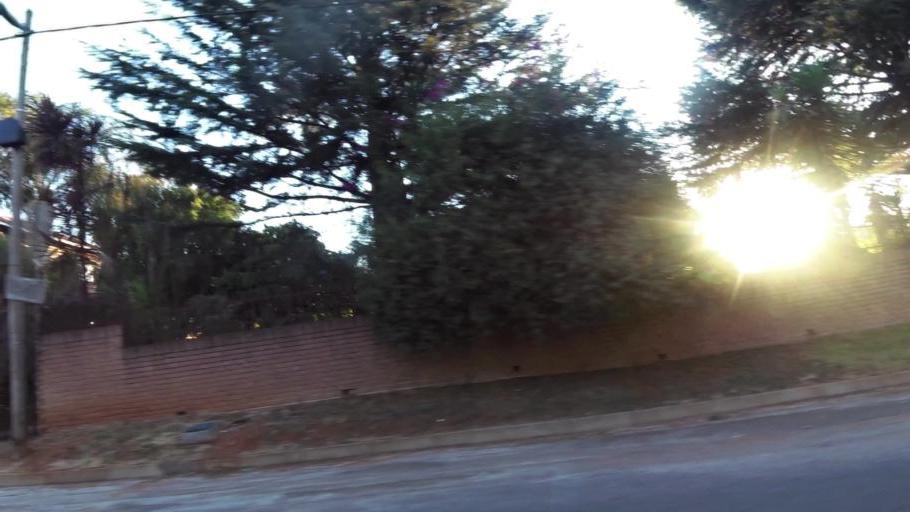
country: ZA
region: Gauteng
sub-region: City of Johannesburg Metropolitan Municipality
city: Roodepoort
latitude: -26.1706
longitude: 27.9579
